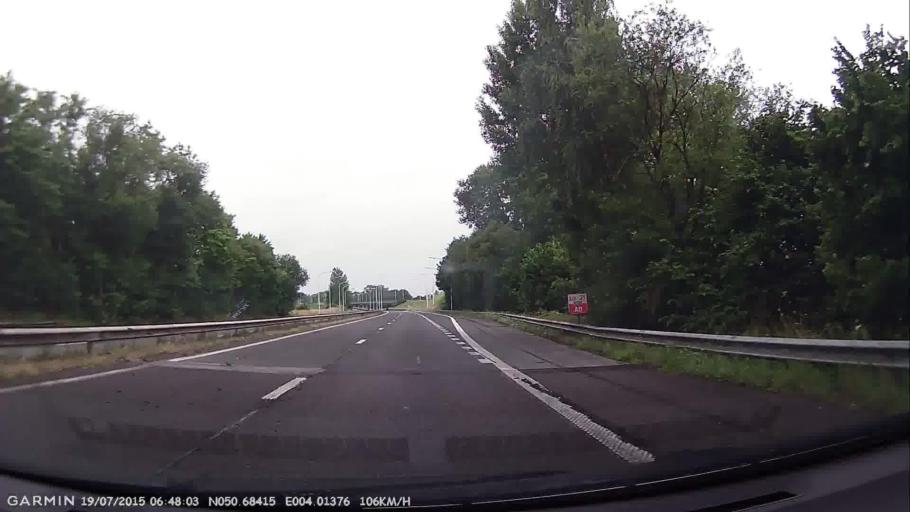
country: BE
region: Wallonia
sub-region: Province du Hainaut
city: Enghien
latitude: 50.6841
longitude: 4.0138
